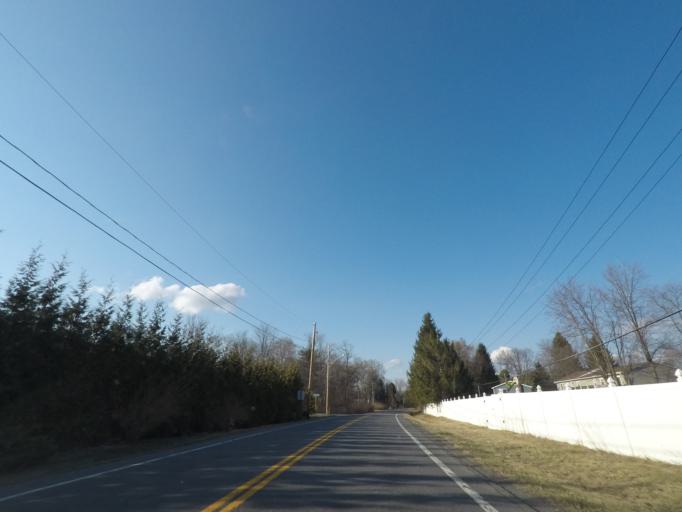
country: US
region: New York
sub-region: Schenectady County
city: Niskayuna
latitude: 42.8208
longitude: -73.7909
